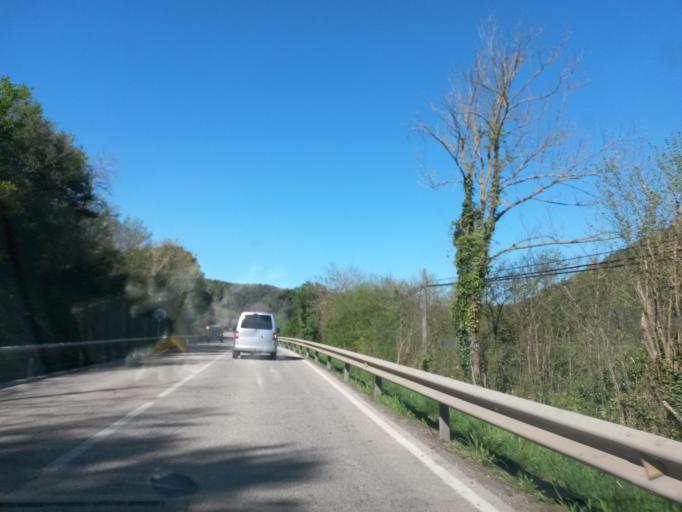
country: ES
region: Catalonia
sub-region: Provincia de Girona
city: Santa Pau
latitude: 42.1497
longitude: 2.5408
